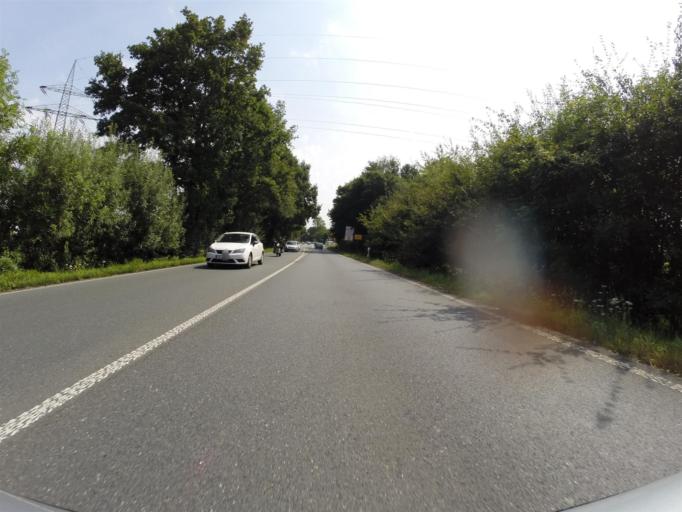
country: DE
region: North Rhine-Westphalia
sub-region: Regierungsbezirk Detmold
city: Herford
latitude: 52.1323
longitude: 8.6661
